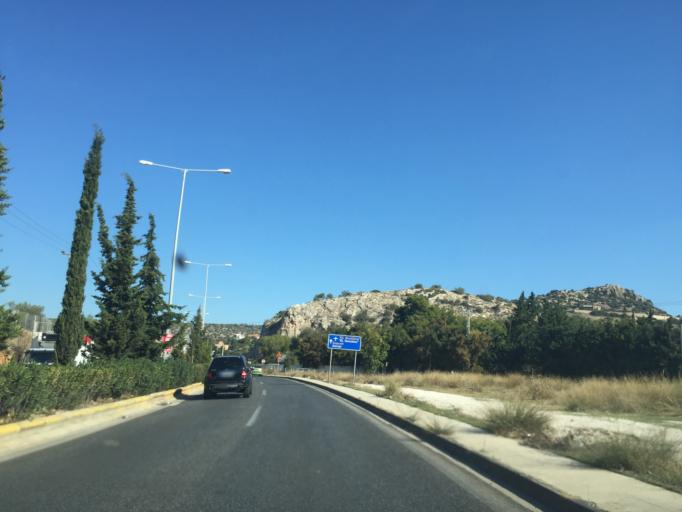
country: GR
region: Attica
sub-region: Nomarchia Anatolikis Attikis
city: Kitsi
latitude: 37.8490
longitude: 23.8287
